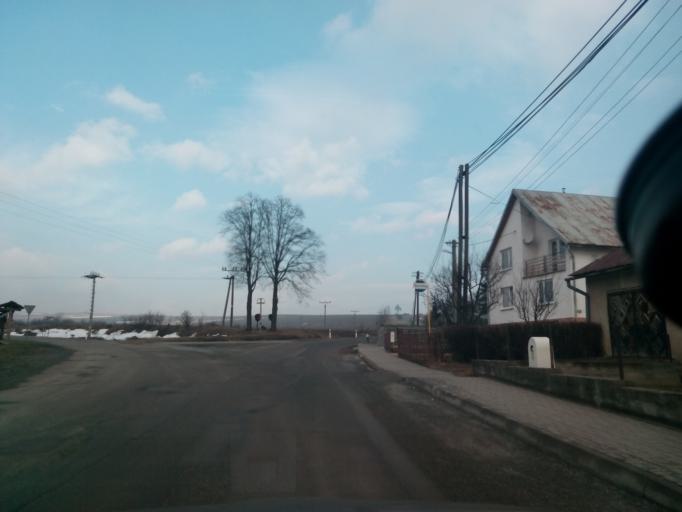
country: SK
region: Presovsky
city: Lipany
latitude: 49.1766
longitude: 20.8557
